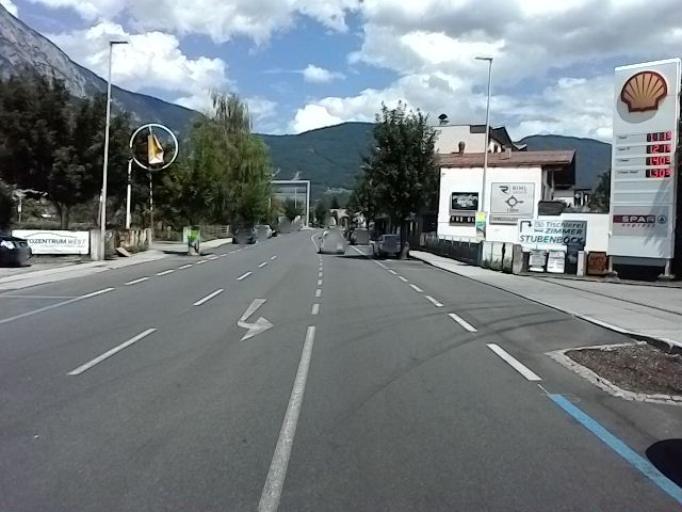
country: AT
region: Tyrol
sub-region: Politischer Bezirk Innsbruck Land
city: Telfs
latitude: 47.3056
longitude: 11.0749
